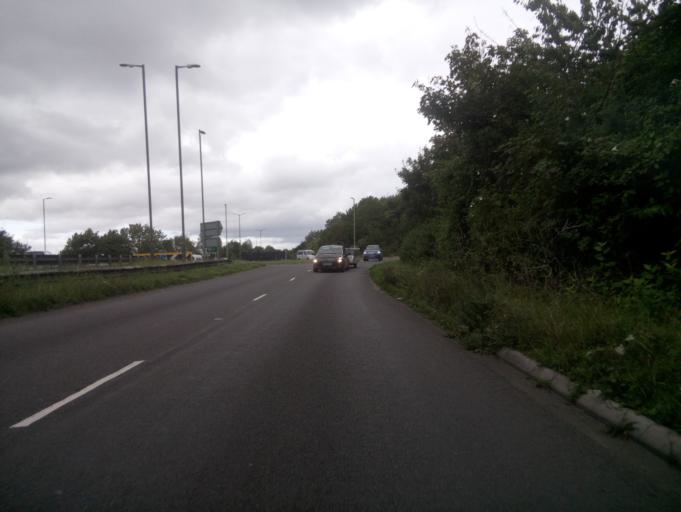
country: GB
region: England
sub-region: Devon
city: Marldon
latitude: 50.4727
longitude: -3.5821
